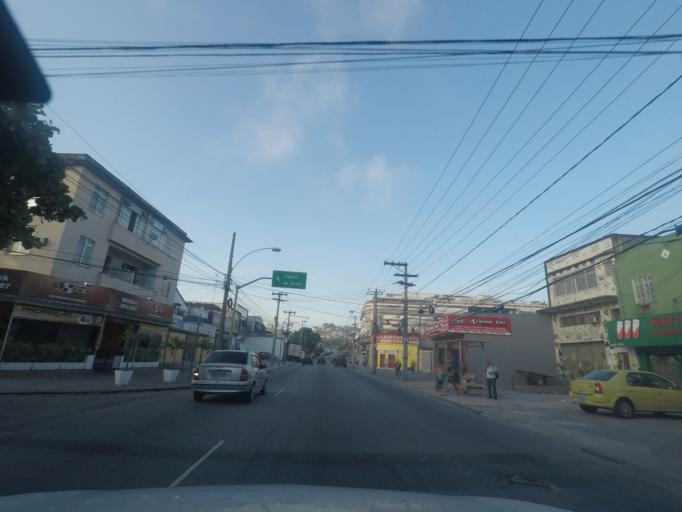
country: BR
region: Rio de Janeiro
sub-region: Duque De Caxias
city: Duque de Caxias
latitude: -22.8335
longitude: -43.2806
